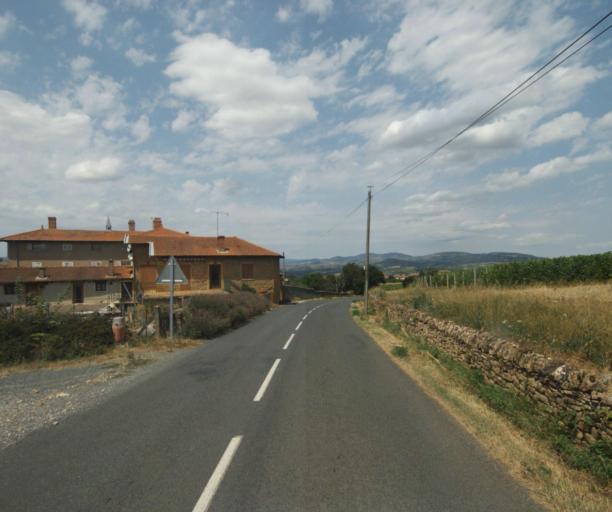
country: FR
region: Rhone-Alpes
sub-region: Departement du Rhone
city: Saint-Germain-Nuelles
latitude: 45.8693
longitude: 4.6043
